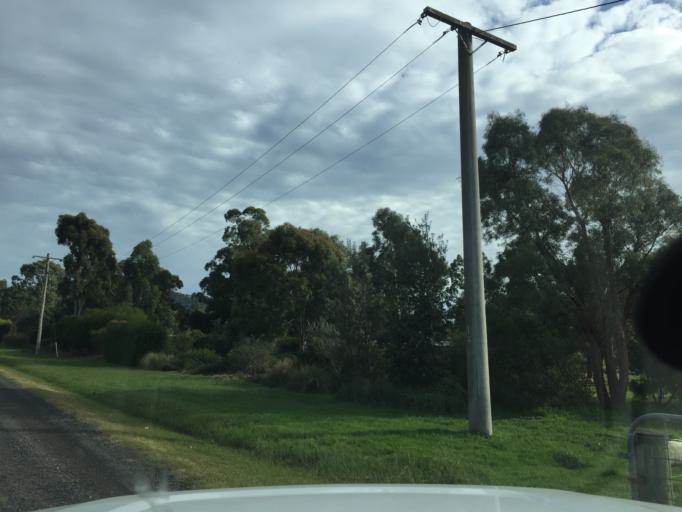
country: AU
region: Victoria
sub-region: Yarra Ranges
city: Yarra Glen
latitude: -37.6399
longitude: 145.3823
